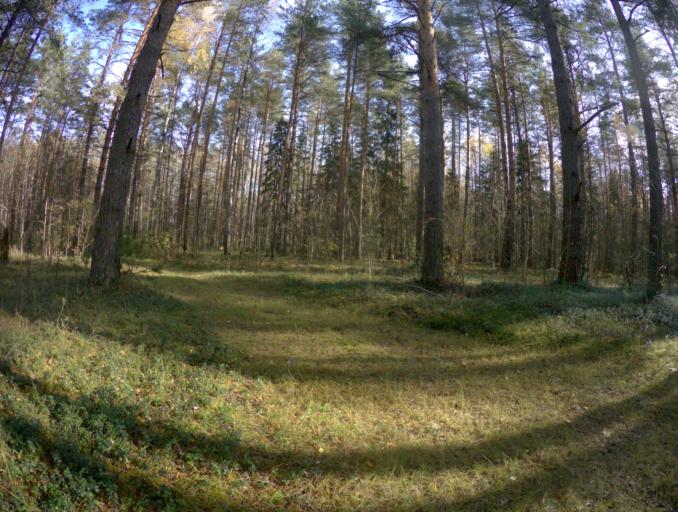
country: RU
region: Vladimir
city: Kommunar
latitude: 56.0818
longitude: 40.4413
